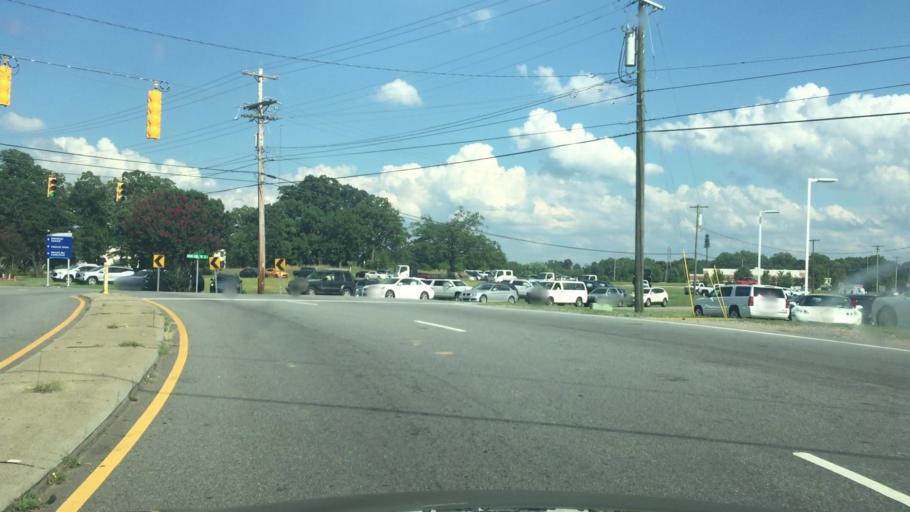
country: US
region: North Carolina
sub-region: Cabarrus County
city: Concord
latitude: 35.3959
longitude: -80.6110
